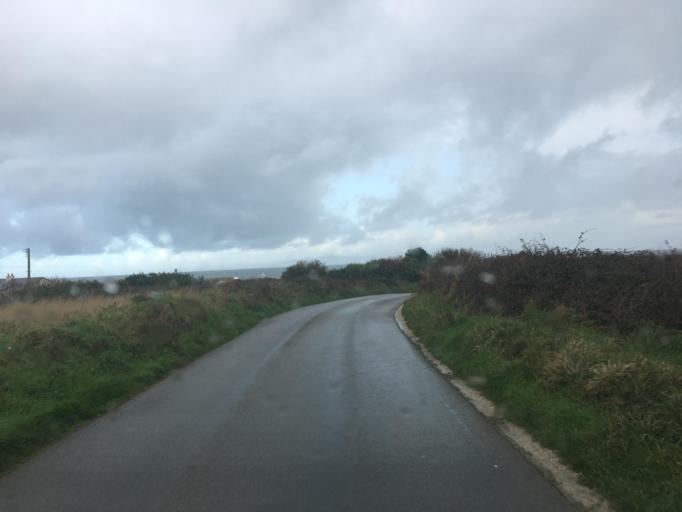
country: FR
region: Lower Normandy
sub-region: Departement de la Manche
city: Reville
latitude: 49.6915
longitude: -1.2777
